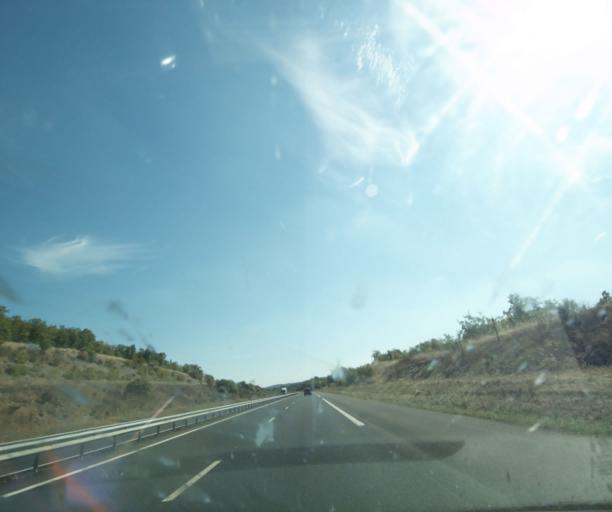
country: FR
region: Limousin
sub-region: Departement de la Correze
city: Brive-la-Gaillarde
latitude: 45.0334
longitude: 1.5263
